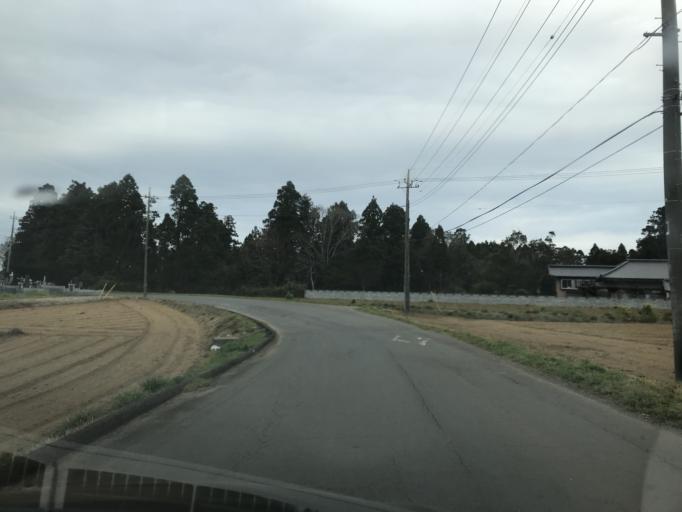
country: JP
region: Chiba
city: Sawara
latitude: 35.8439
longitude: 140.4858
